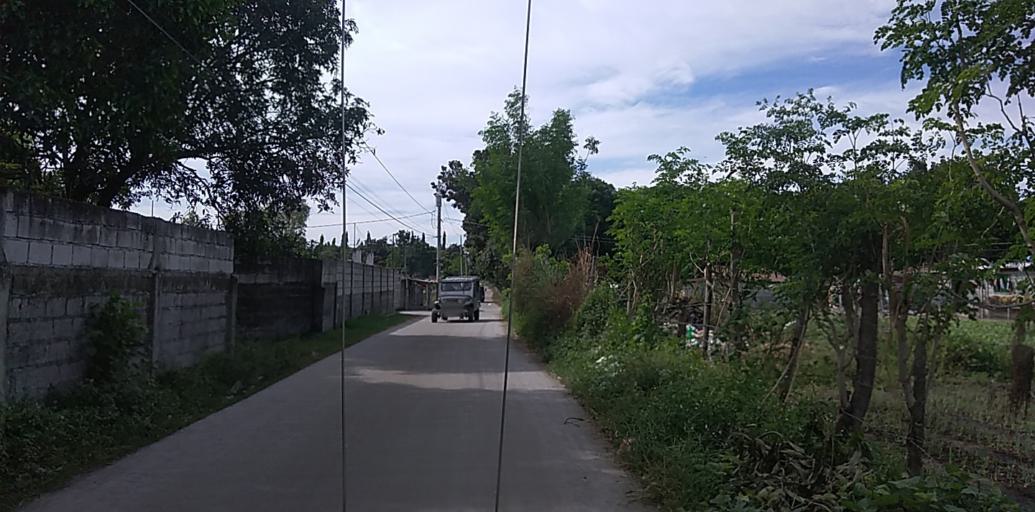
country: PH
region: Central Luzon
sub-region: Province of Pampanga
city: Angeles City
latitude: 15.1272
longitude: 120.5642
